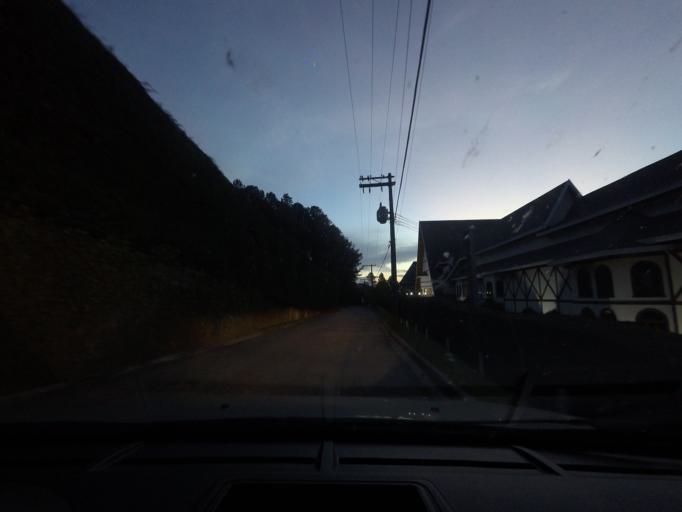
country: BR
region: Sao Paulo
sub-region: Campos Do Jordao
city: Campos do Jordao
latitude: -22.7519
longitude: -45.5564
